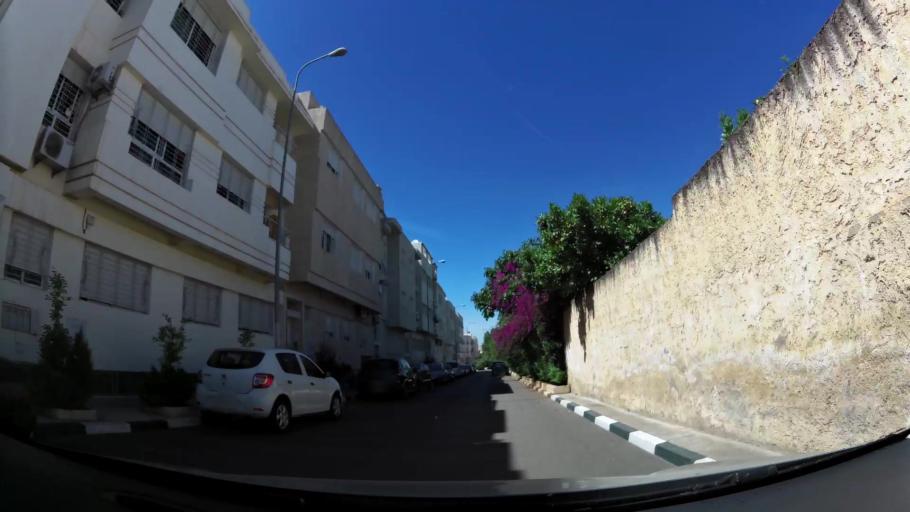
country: MA
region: Fes-Boulemane
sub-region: Fes
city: Fes
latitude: 34.0160
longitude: -5.0006
